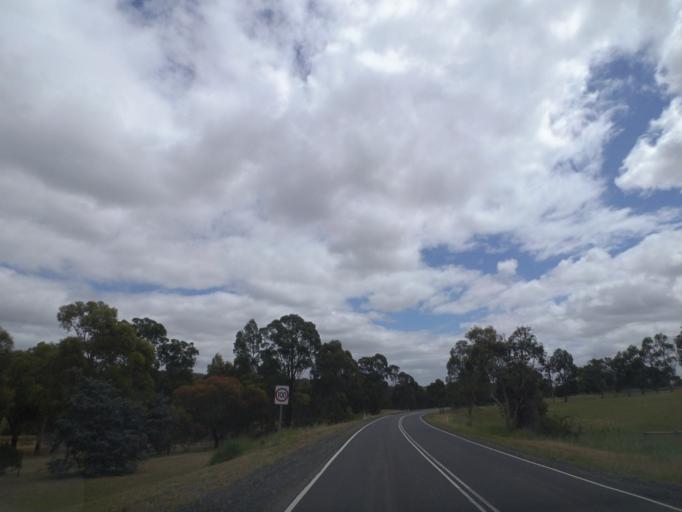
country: AU
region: Victoria
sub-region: Whittlesea
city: Whittlesea
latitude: -37.2844
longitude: 145.0518
